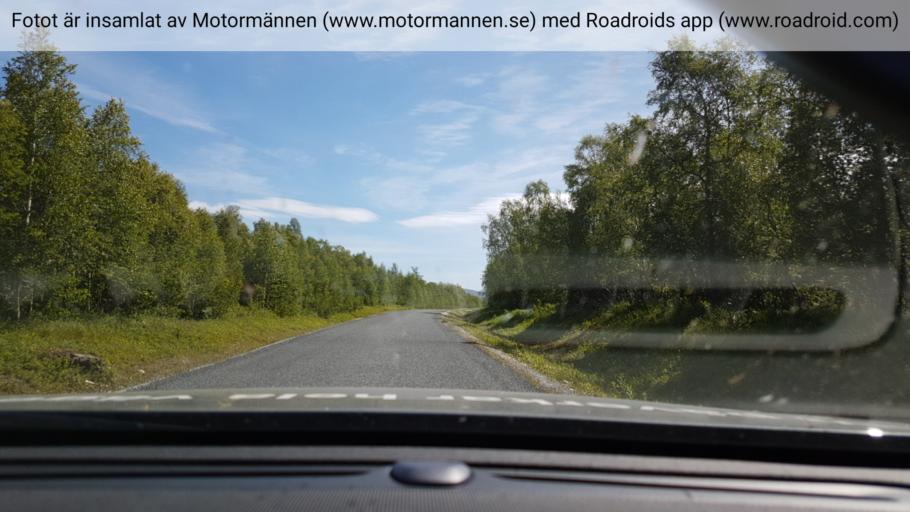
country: NO
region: Nordland
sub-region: Hattfjelldal
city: Hattfjelldal
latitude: 65.3362
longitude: 15.1222
